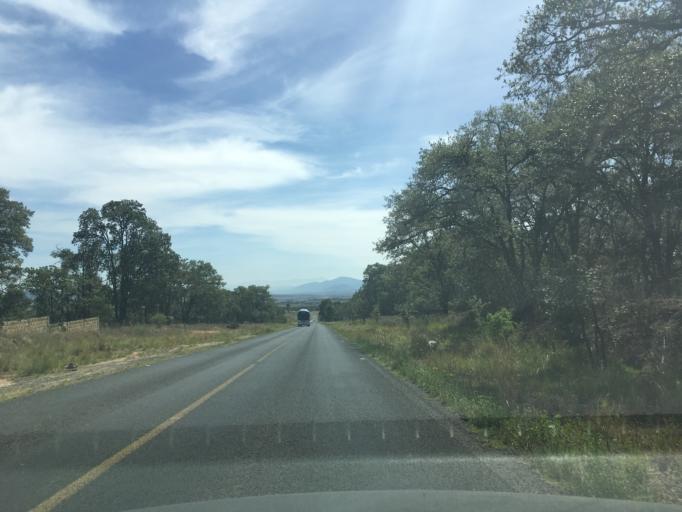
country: MX
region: Queretaro
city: Amealco
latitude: 20.2245
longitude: -100.0961
